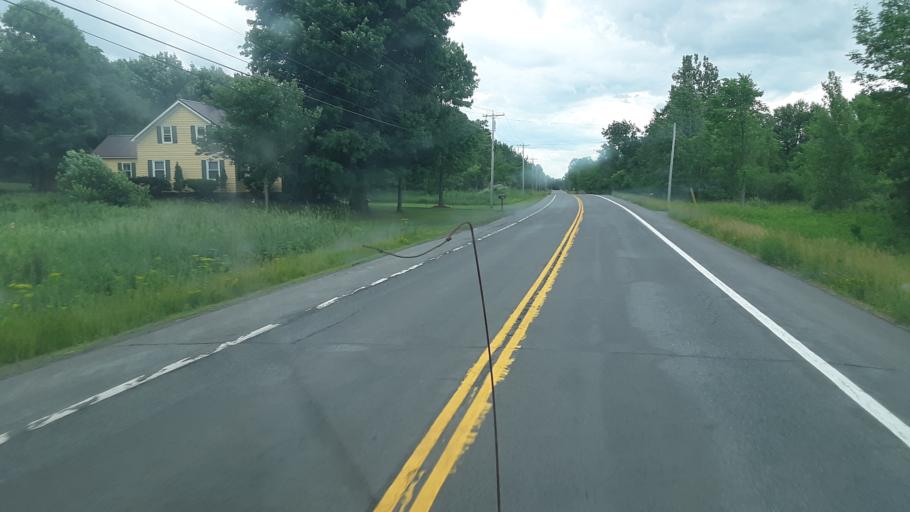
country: US
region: New York
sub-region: Oneida County
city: Rome
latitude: 43.3459
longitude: -75.4761
